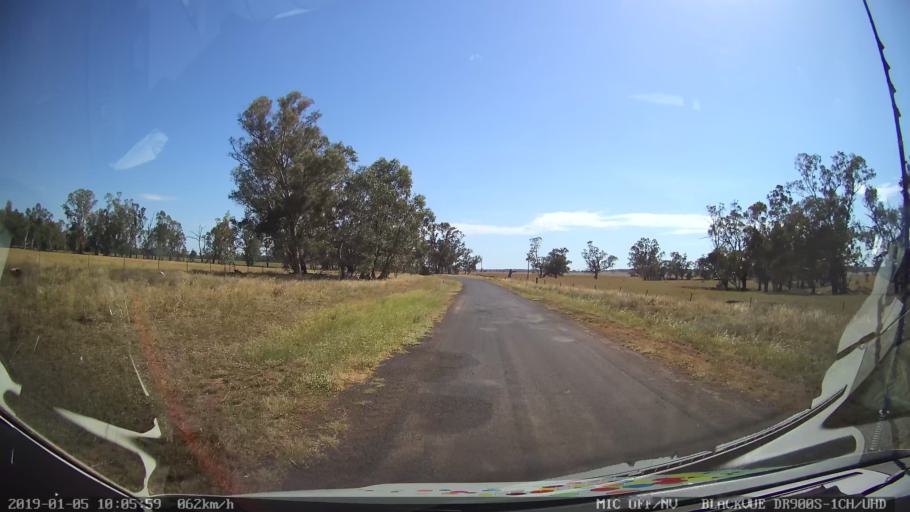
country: AU
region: New South Wales
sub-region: Gilgandra
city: Gilgandra
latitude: -31.6614
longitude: 148.8682
